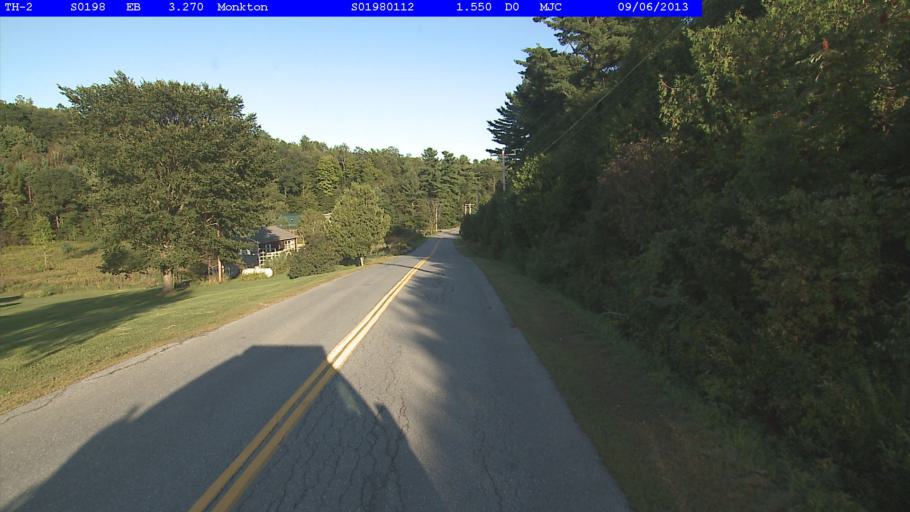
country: US
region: Vermont
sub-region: Chittenden County
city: Hinesburg
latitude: 44.2463
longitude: -73.1694
